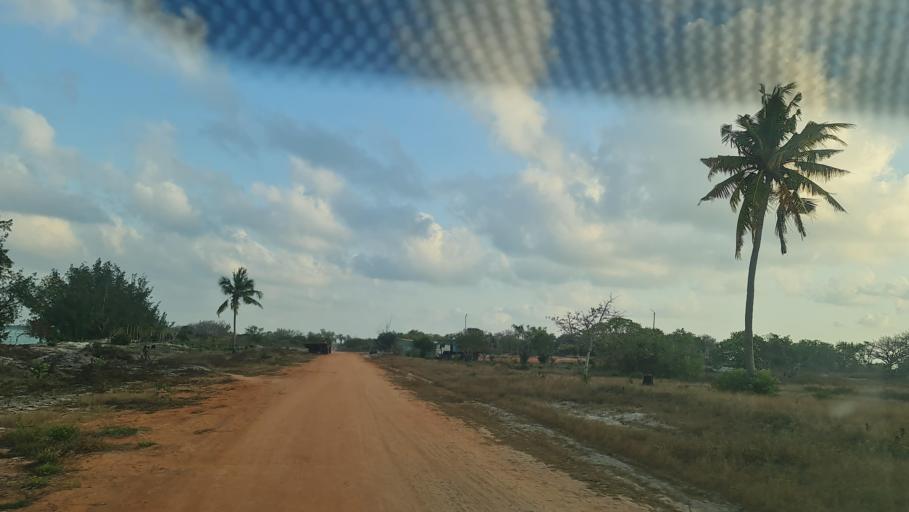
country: MZ
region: Nampula
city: Ilha de Mocambique
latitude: -14.7866
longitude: 40.8210
